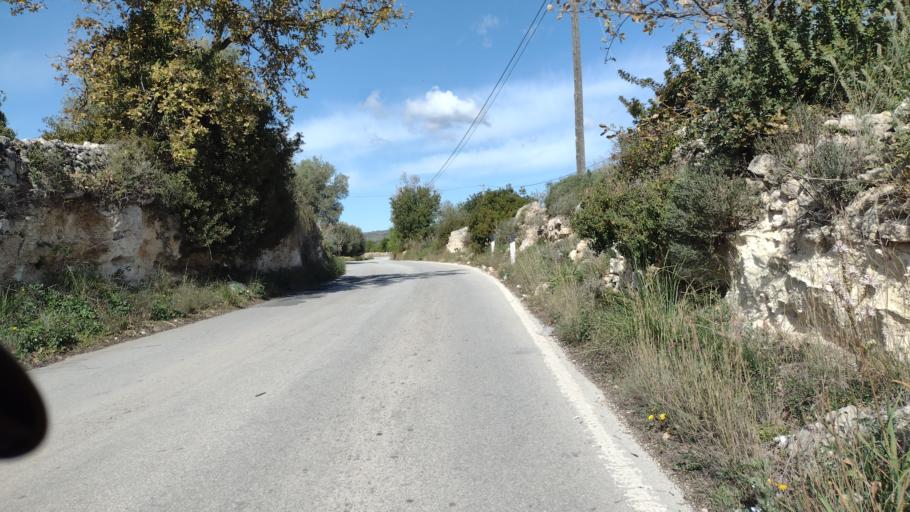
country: IT
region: Sicily
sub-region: Provincia di Siracusa
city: Noto
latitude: 36.8879
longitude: 15.0513
